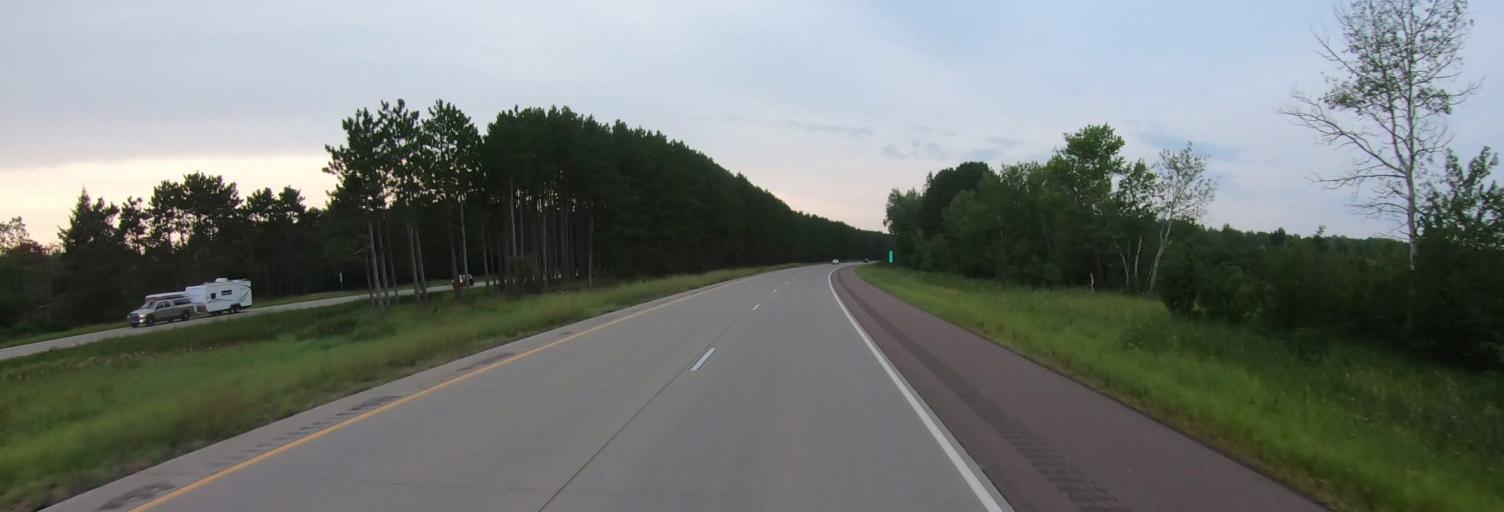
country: US
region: Minnesota
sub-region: Pine County
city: Sandstone
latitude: 46.1487
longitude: -92.8863
